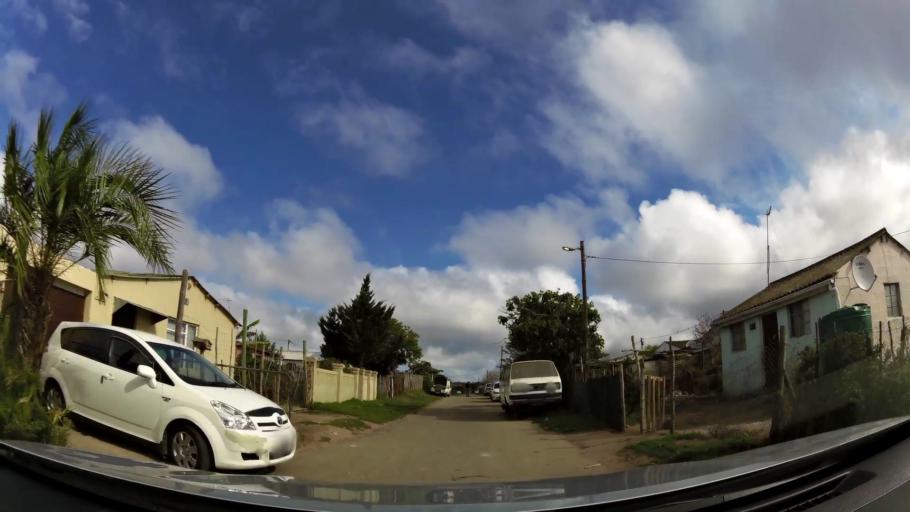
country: ZA
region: Western Cape
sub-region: Eden District Municipality
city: Plettenberg Bay
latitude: -34.0489
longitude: 23.3267
